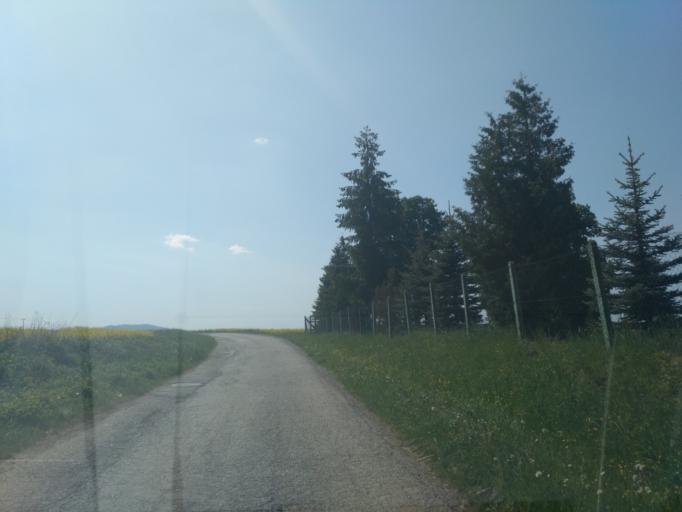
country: SK
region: Kosicky
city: Kosice
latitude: 48.8511
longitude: 21.4282
